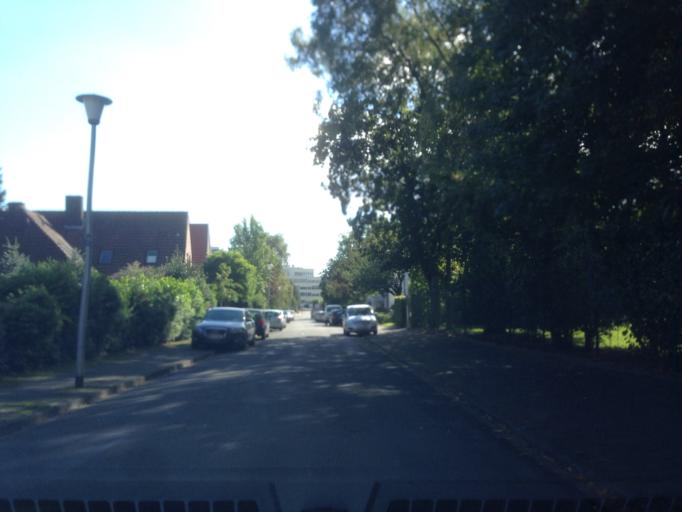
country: DE
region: North Rhine-Westphalia
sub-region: Regierungsbezirk Munster
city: Muenster
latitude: 51.9667
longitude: 7.5947
